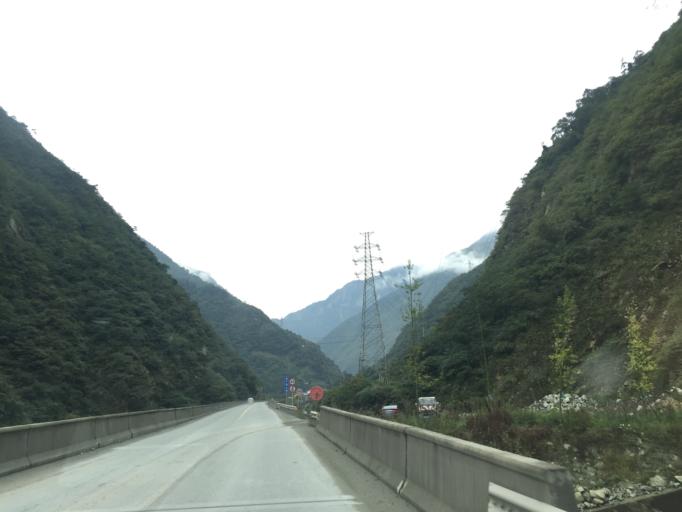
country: CN
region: Sichuan
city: Guangsheng
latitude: 31.0685
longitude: 103.4761
